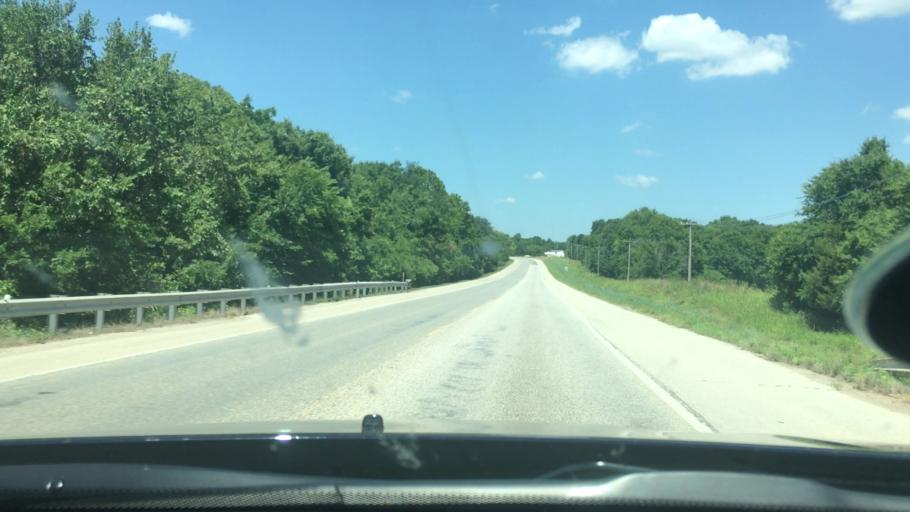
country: US
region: Oklahoma
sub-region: Marshall County
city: Oakland
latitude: 34.1821
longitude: -96.8680
